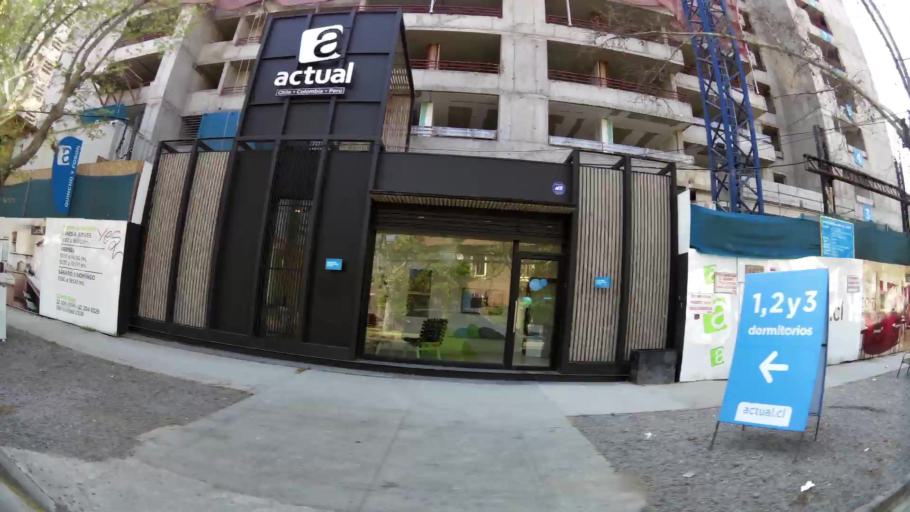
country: CL
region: Santiago Metropolitan
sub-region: Provincia de Santiago
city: Santiago
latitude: -33.4545
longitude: -70.6166
